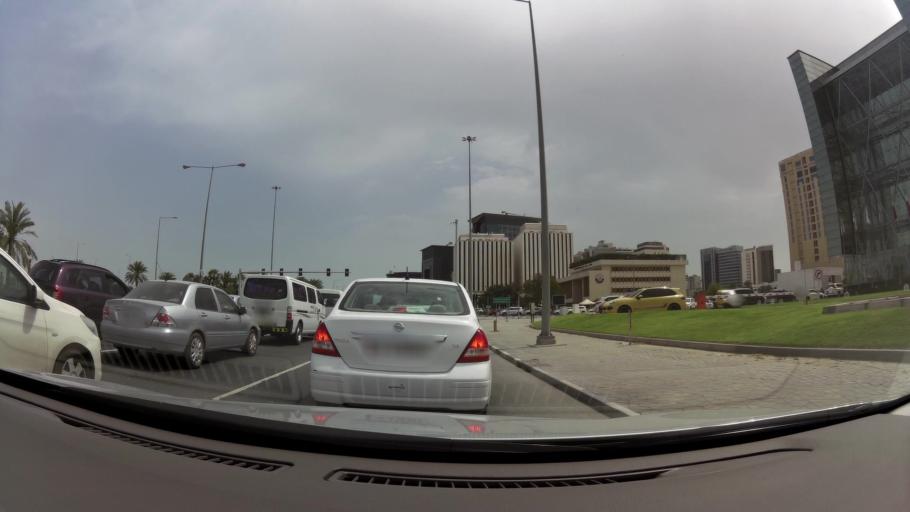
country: QA
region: Baladiyat ad Dawhah
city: Doha
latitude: 25.2909
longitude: 51.5384
